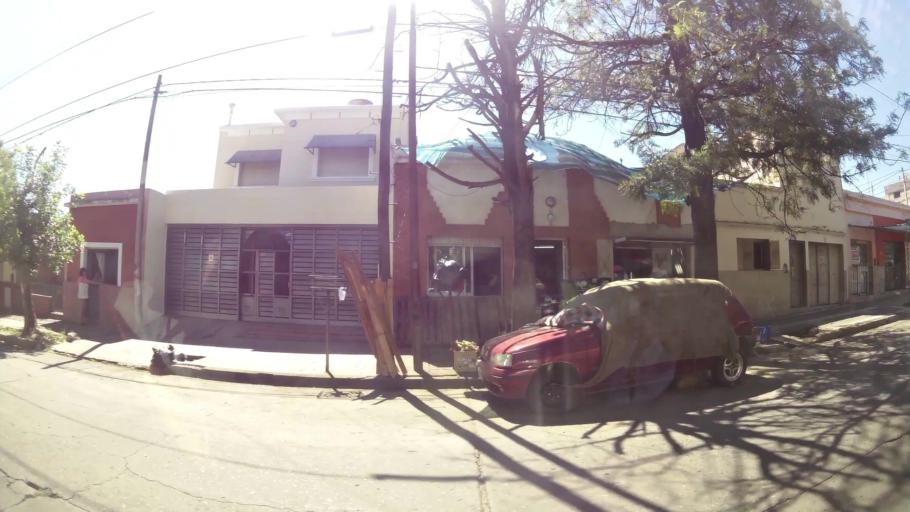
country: AR
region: Cordoba
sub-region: Departamento de Capital
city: Cordoba
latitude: -31.4254
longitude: -64.1584
